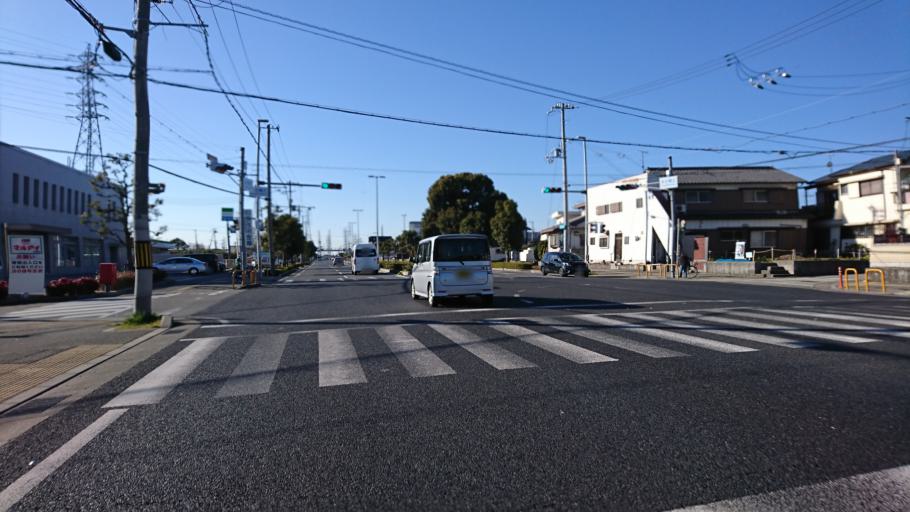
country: JP
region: Hyogo
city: Kakogawacho-honmachi
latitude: 34.7776
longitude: 134.8131
